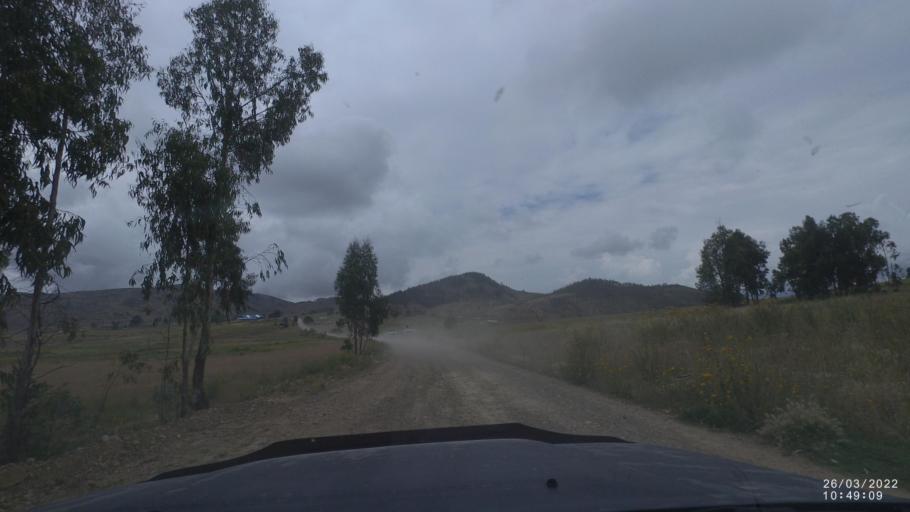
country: BO
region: Cochabamba
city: Tarata
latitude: -17.5009
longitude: -66.0403
